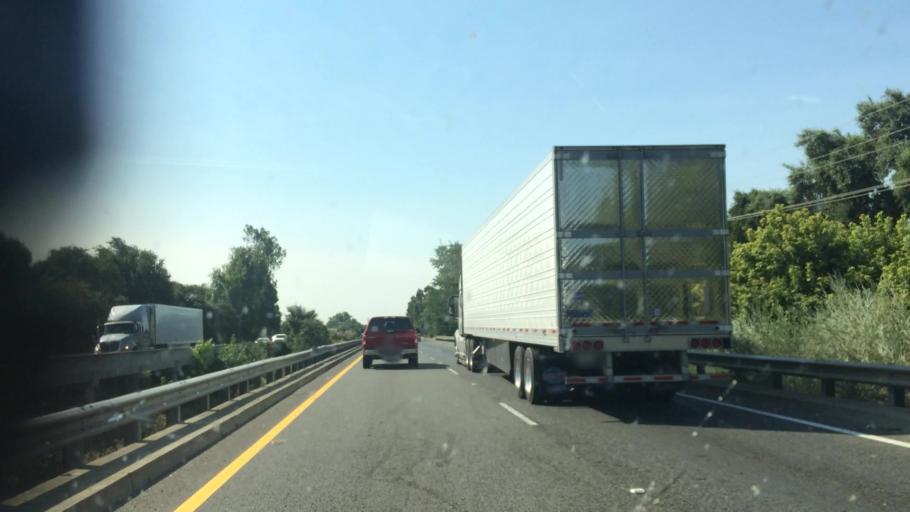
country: US
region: California
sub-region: Sacramento County
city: Elk Grove
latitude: 38.3519
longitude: -121.3404
